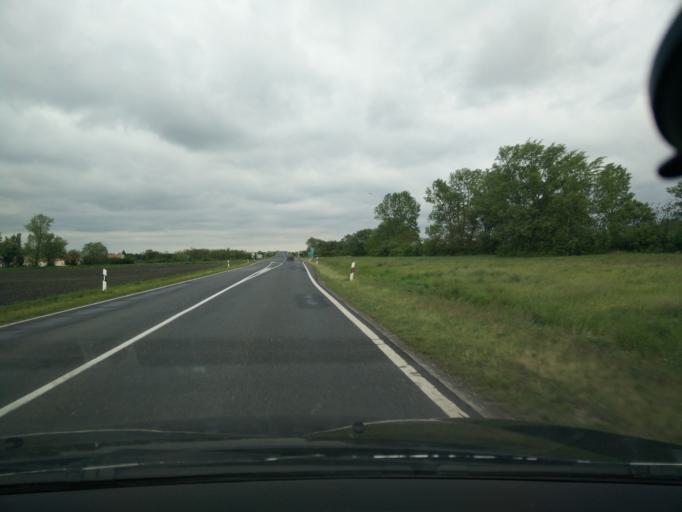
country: HU
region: Veszprem
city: Papa
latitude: 47.3386
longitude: 17.4396
